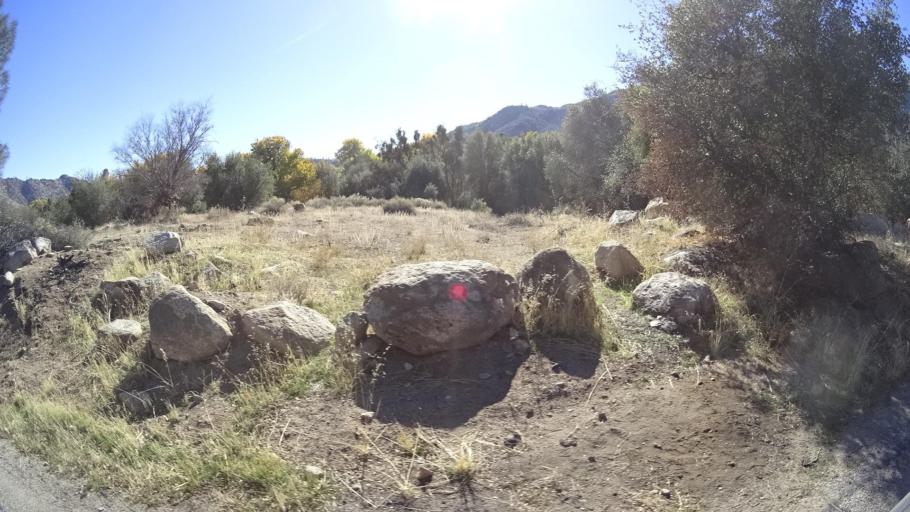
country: US
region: California
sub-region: Kern County
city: Kernville
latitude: 35.7678
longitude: -118.4281
